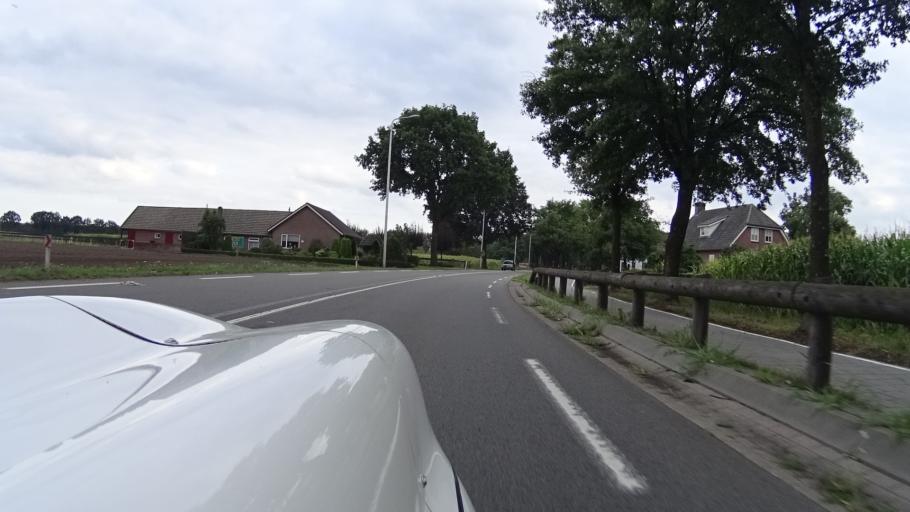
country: NL
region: North Brabant
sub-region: Gemeente Boekel
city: Boekel
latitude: 51.5809
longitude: 5.6908
